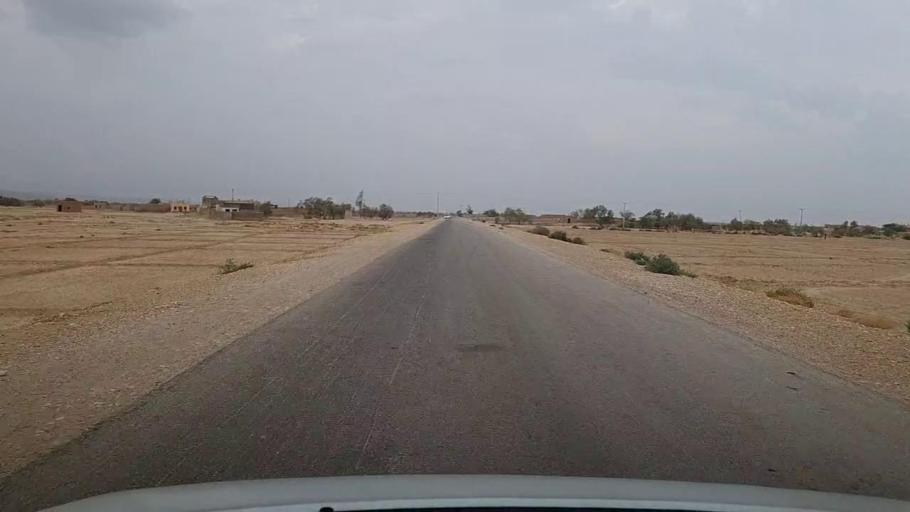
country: PK
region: Sindh
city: Sehwan
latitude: 26.3356
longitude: 67.7186
